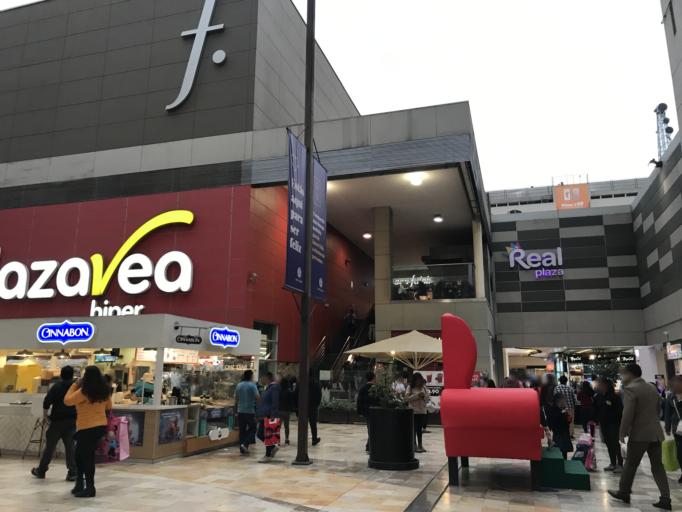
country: PE
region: Lima
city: Lima
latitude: -12.0570
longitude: -77.0372
